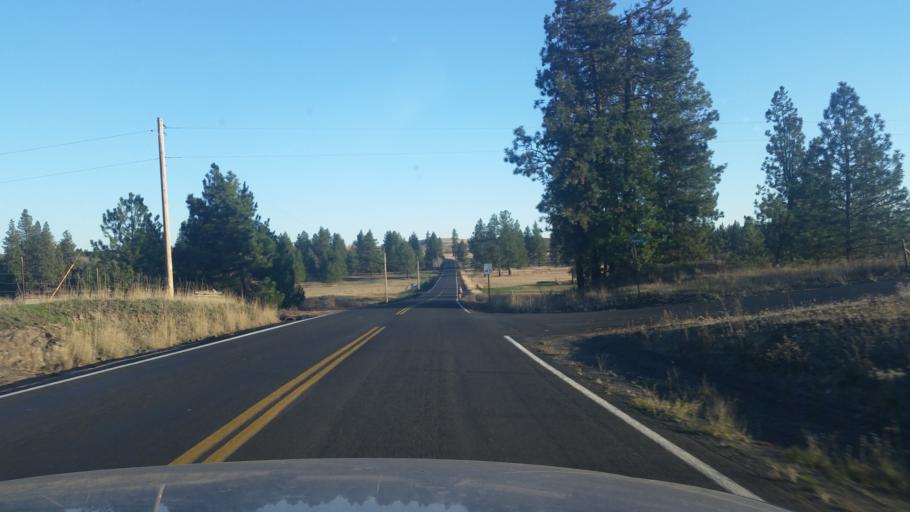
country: US
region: Washington
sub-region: Spokane County
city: Opportunity
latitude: 47.3836
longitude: -117.3162
